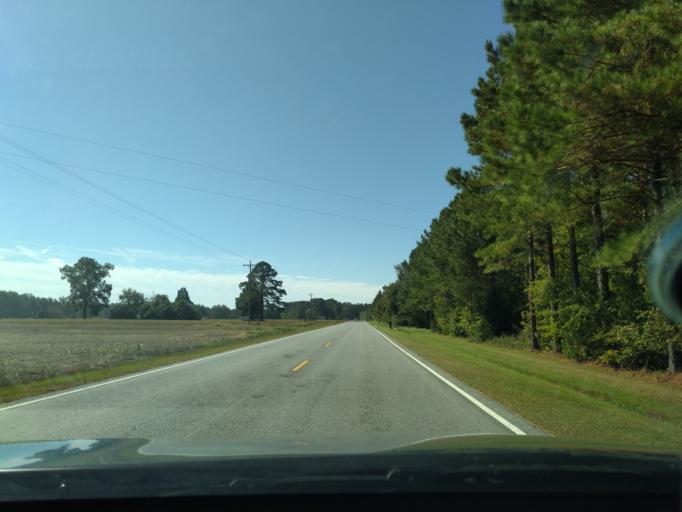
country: US
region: North Carolina
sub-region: Washington County
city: Plymouth
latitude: 35.6835
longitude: -76.7790
